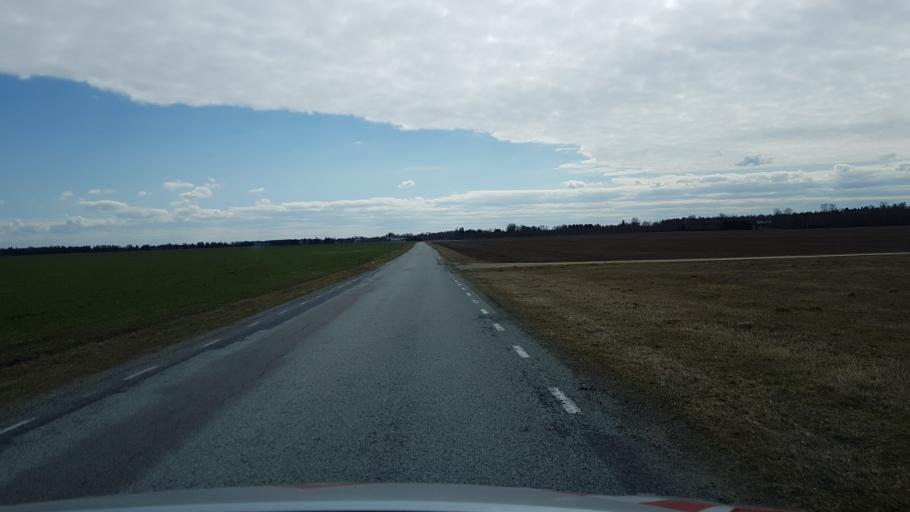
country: EE
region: Laeaene-Virumaa
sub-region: Haljala vald
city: Haljala
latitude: 59.4126
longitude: 26.2527
